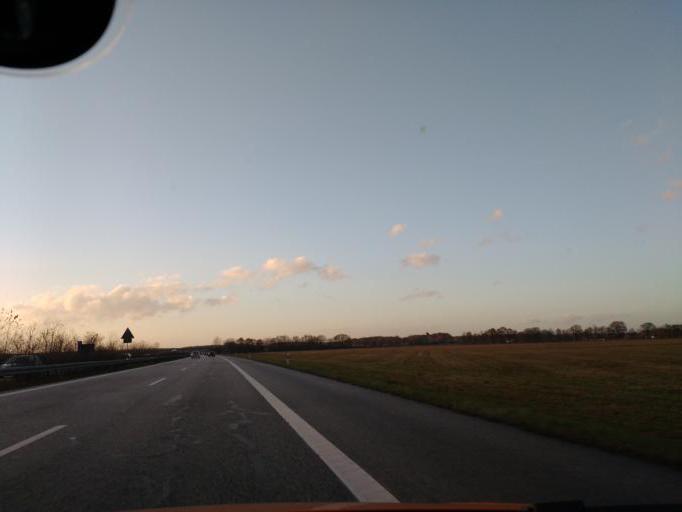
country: DE
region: Mecklenburg-Vorpommern
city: Sulstorf
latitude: 53.4689
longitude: 11.3265
